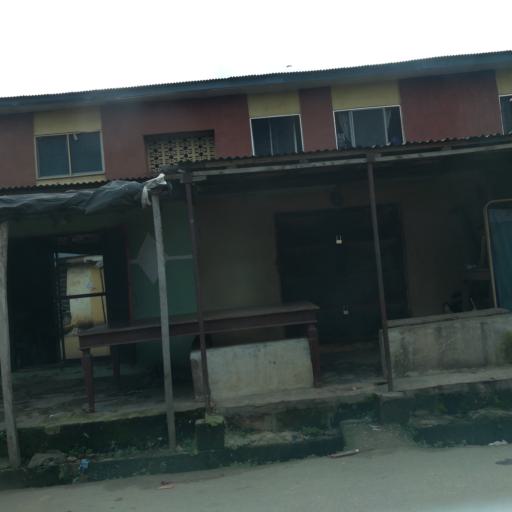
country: NG
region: Lagos
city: Agege
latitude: 6.6084
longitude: 3.2965
